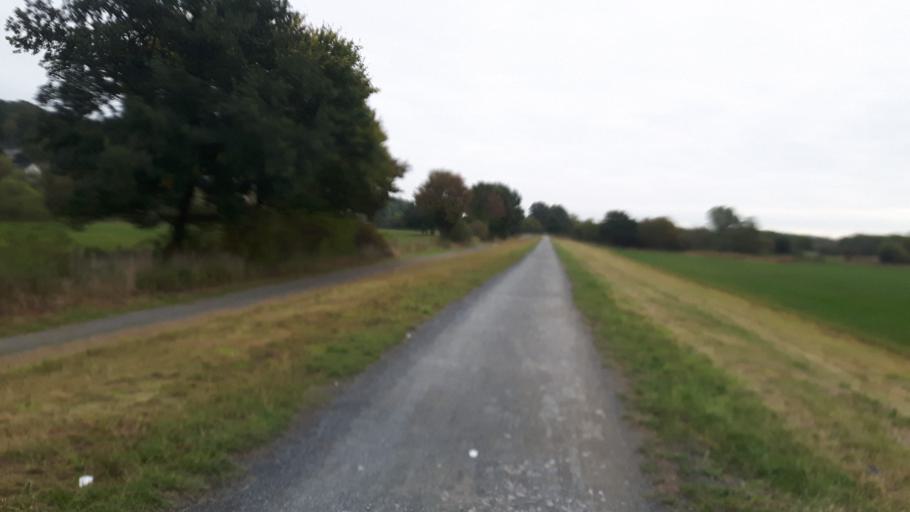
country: DE
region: North Rhine-Westphalia
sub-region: Regierungsbezirk Koln
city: Hennef
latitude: 50.7899
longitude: 7.2756
